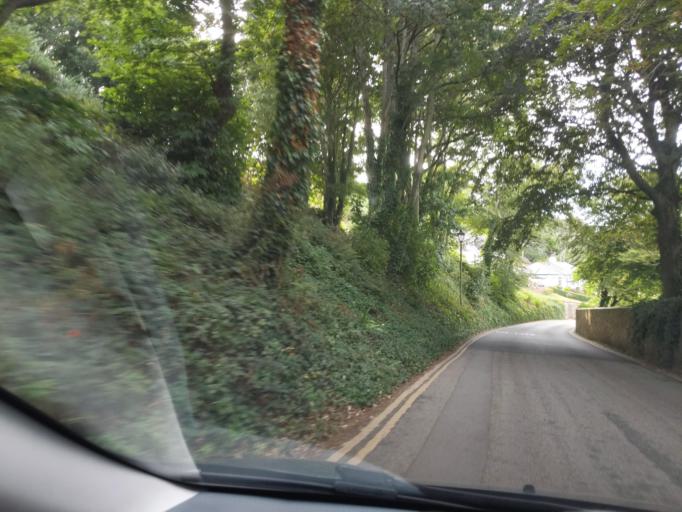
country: GB
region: England
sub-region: Cornwall
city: Millbrook
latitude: 50.3331
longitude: -4.2028
